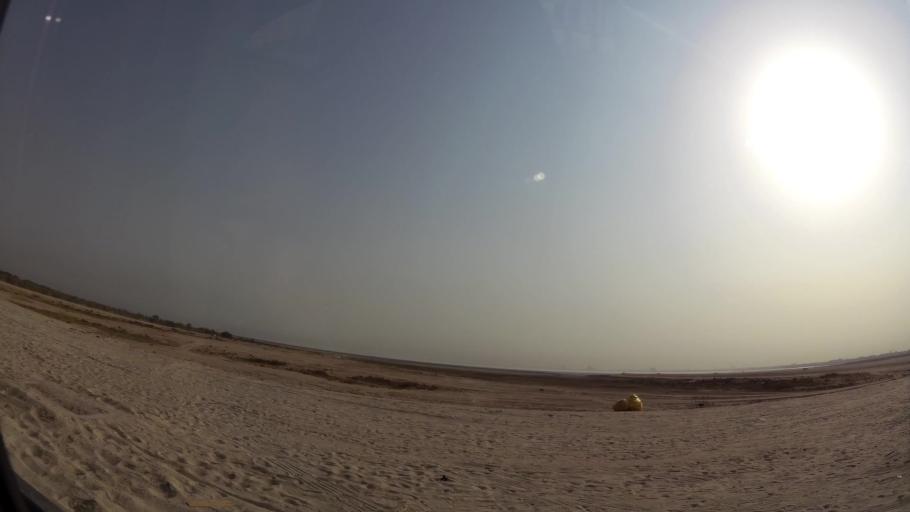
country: KW
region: Al Asimah
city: Ar Rabiyah
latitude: 29.3328
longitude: 47.8154
